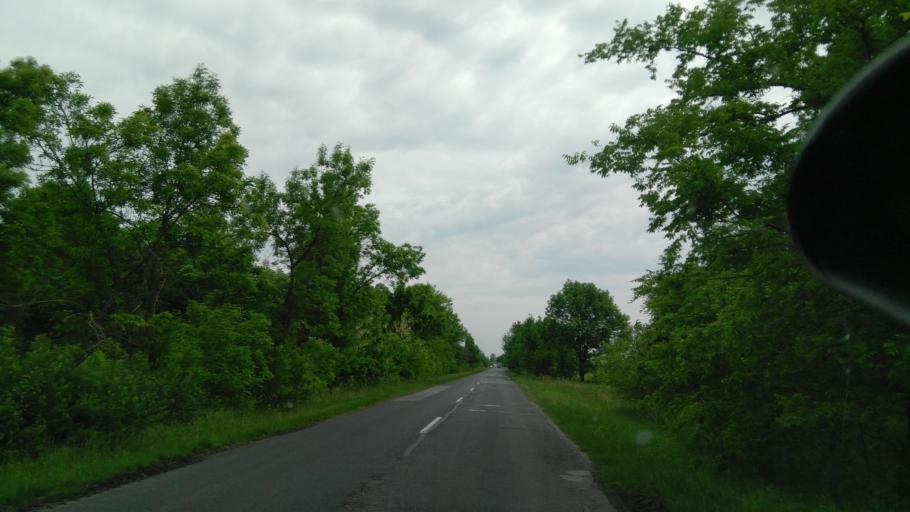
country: HU
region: Bekes
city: Szeghalom
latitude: 47.0058
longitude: 21.1779
